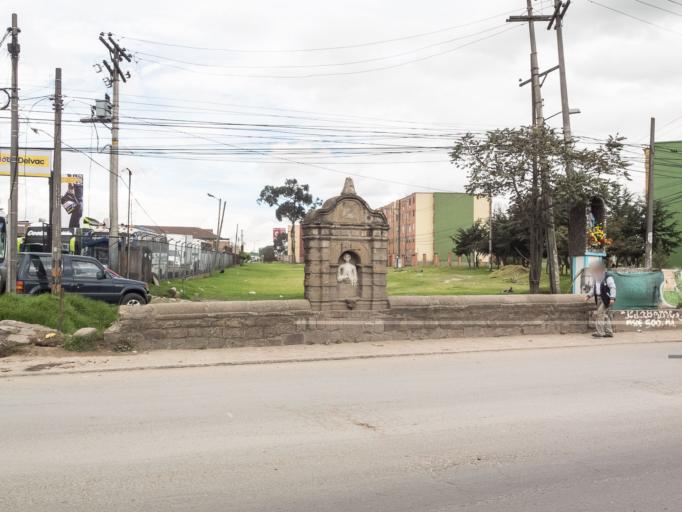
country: CO
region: Bogota D.C.
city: Bogota
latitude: 4.6656
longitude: -74.1407
